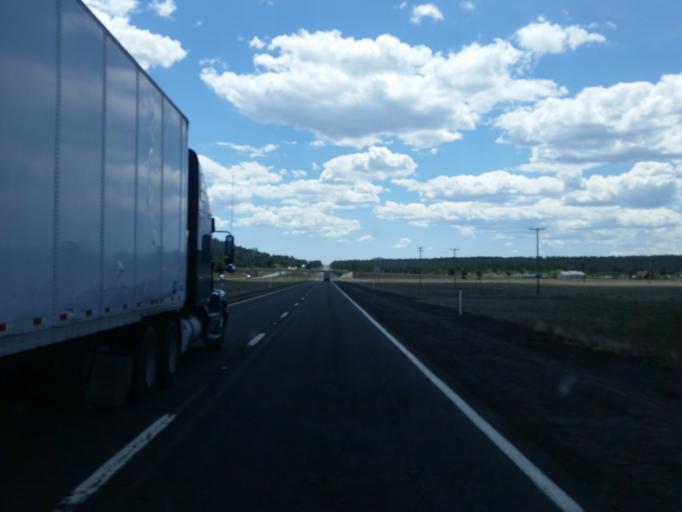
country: US
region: Arizona
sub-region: Coconino County
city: Parks
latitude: 35.2615
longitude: -112.0384
